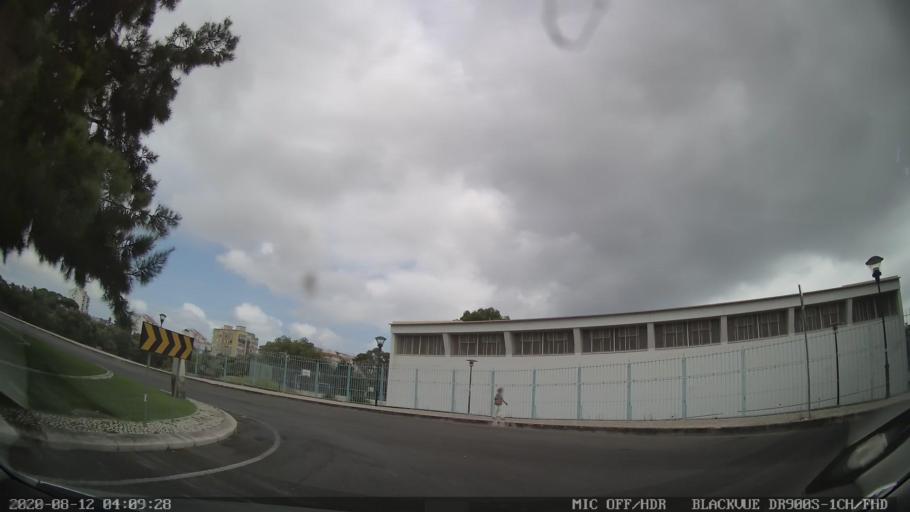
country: PT
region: Lisbon
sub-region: Cascais
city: Estoril
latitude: 38.7036
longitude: -9.3837
